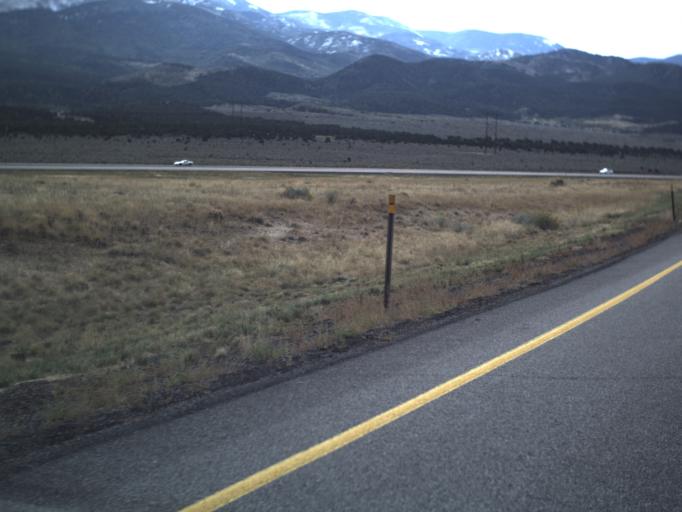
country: US
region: Utah
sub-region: Beaver County
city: Beaver
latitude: 38.5725
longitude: -112.6065
